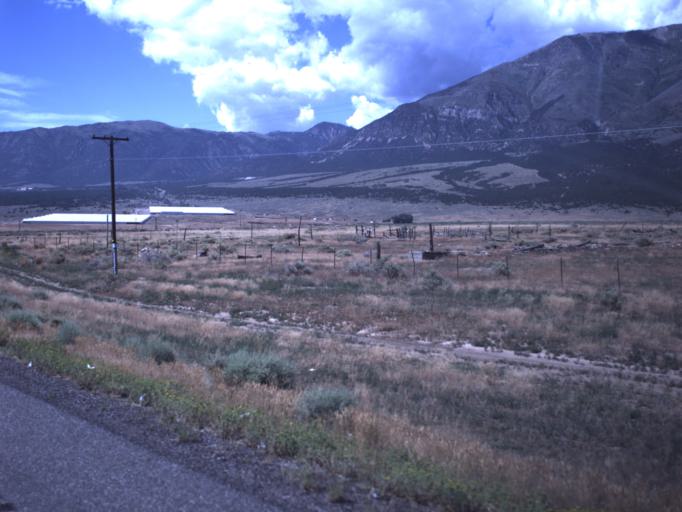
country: US
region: Utah
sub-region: Piute County
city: Junction
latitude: 38.4173
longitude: -112.2315
